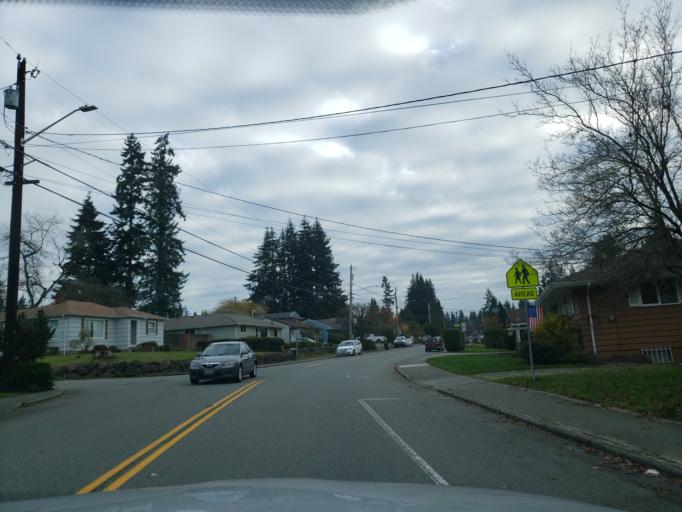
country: US
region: Washington
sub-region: Snohomish County
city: Everett
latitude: 47.9411
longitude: -122.2297
